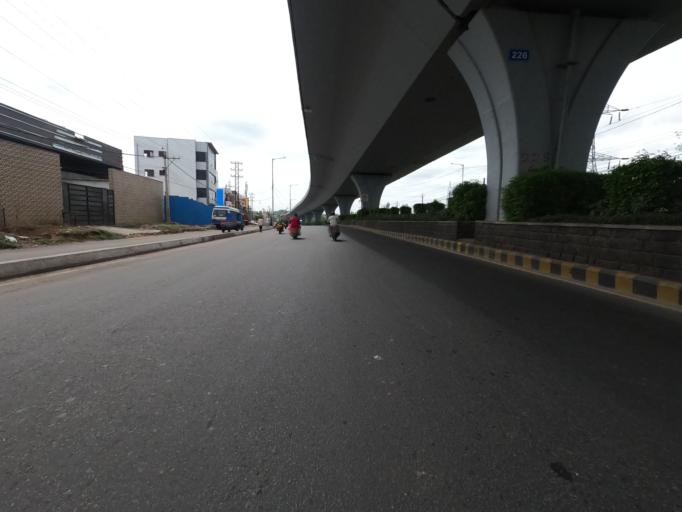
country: IN
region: Telangana
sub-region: Hyderabad
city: Hyderabad
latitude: 17.3432
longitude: 78.4181
